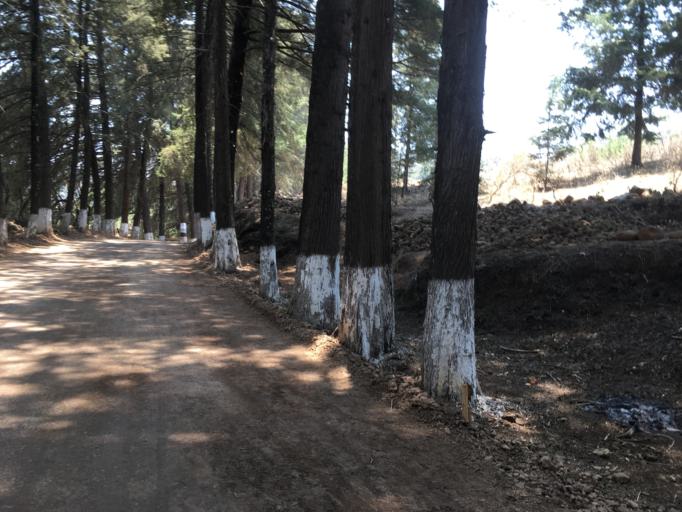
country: MX
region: Michoacan
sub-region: Patzcuaro
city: Santa Ana Chapitiro
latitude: 19.5131
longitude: -101.6343
